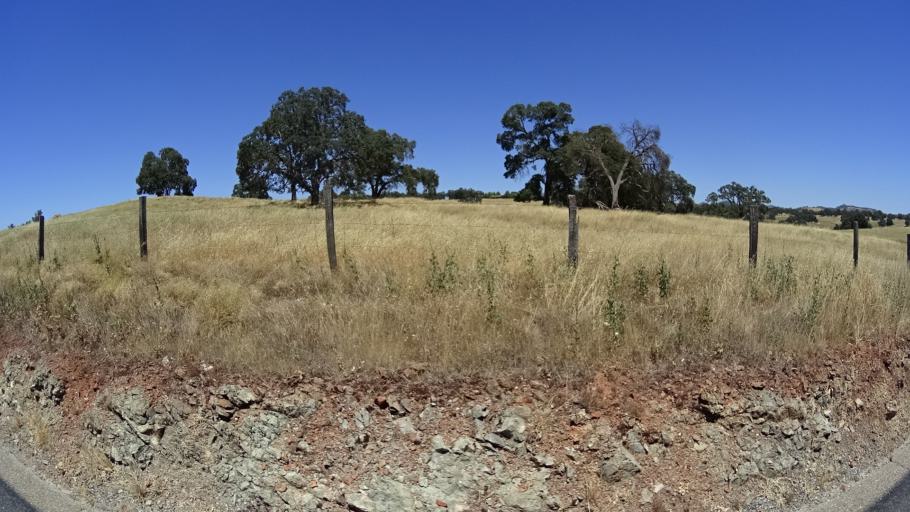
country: US
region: California
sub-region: Calaveras County
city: San Andreas
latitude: 38.1878
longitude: -120.6888
